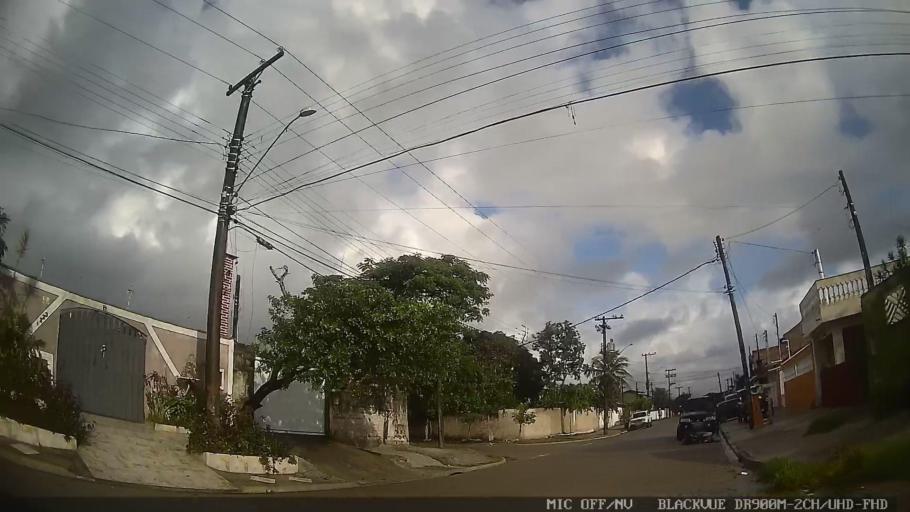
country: BR
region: Sao Paulo
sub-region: Itanhaem
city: Itanhaem
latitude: -24.1843
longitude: -46.8576
